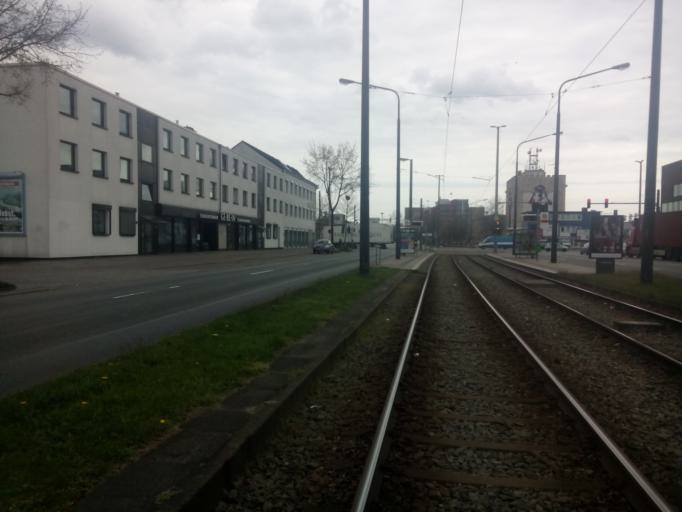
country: DE
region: Bremen
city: Bremen
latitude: 53.0894
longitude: 8.7842
